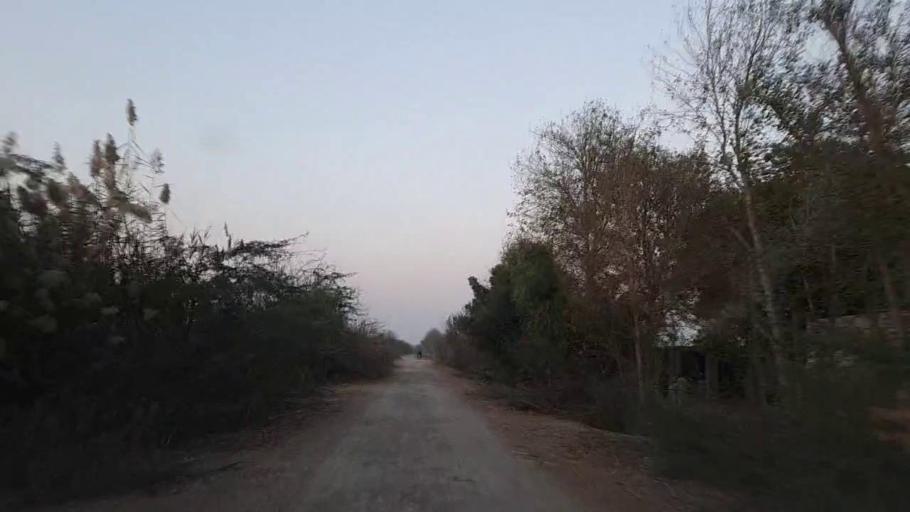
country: PK
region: Sindh
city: Bandhi
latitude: 26.6077
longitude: 68.3750
